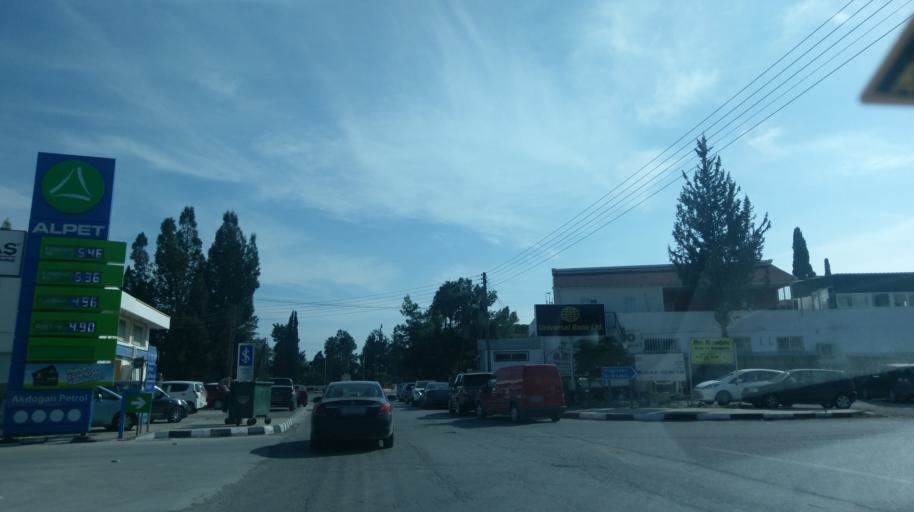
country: CY
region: Larnaka
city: Pergamos
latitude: 35.1102
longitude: 33.6786
